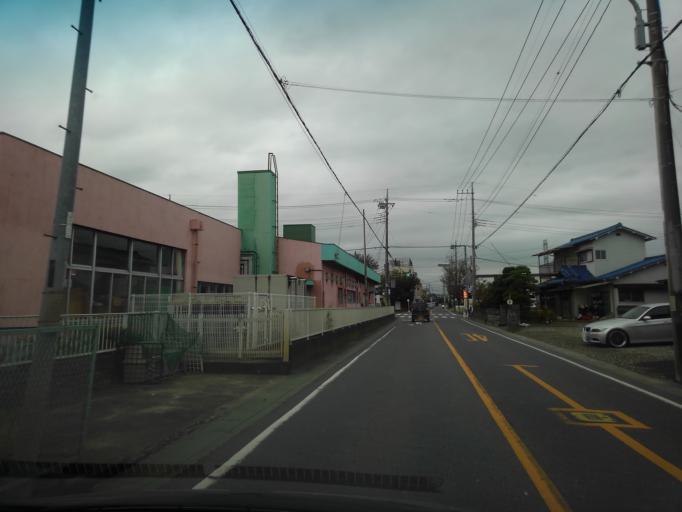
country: JP
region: Saitama
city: Sayama
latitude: 35.7925
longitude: 139.3780
